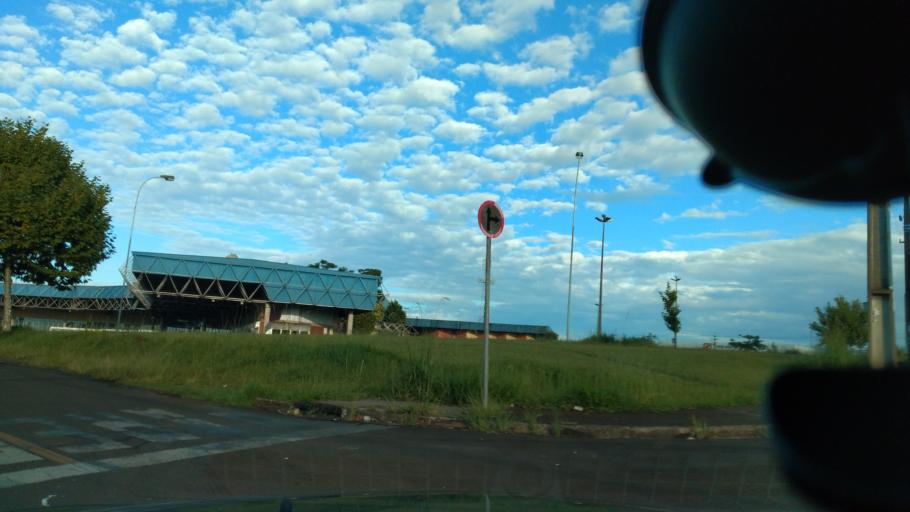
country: BR
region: Parana
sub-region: Guarapuava
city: Guarapuava
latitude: -25.3785
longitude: -51.4762
